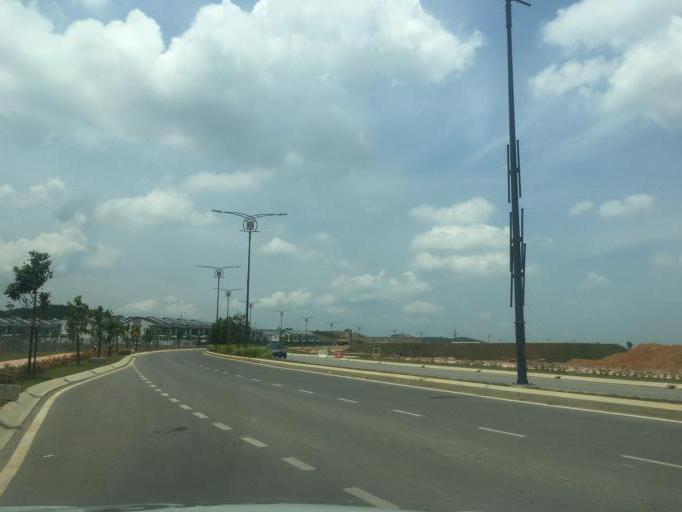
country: MY
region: Putrajaya
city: Putrajaya
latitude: 2.8567
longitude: 101.7037
